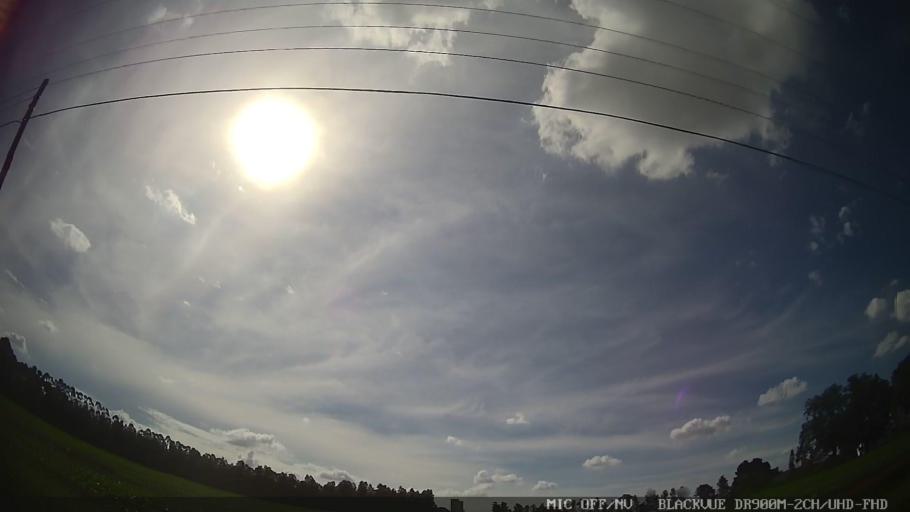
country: BR
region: Sao Paulo
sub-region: Artur Nogueira
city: Artur Nogueira
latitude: -22.6333
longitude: -47.0865
